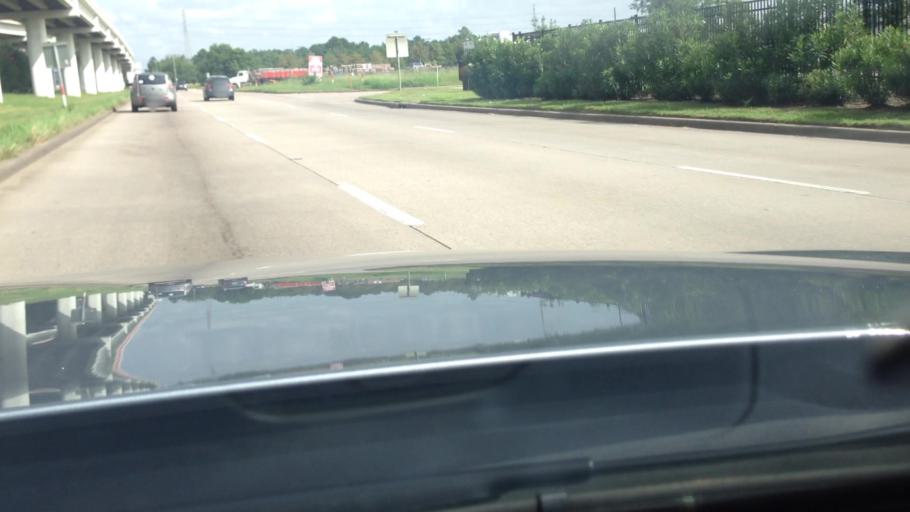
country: US
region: Texas
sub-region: Harris County
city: Hudson
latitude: 29.9384
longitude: -95.5174
